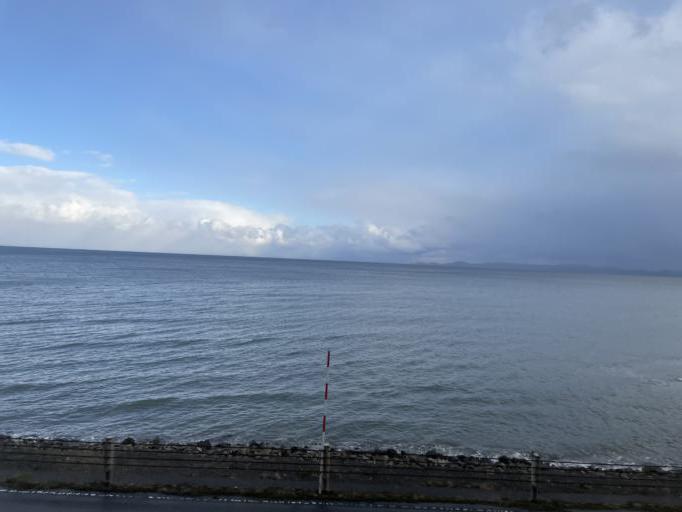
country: JP
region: Aomori
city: Aomori Shi
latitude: 41.0277
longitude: 140.6467
